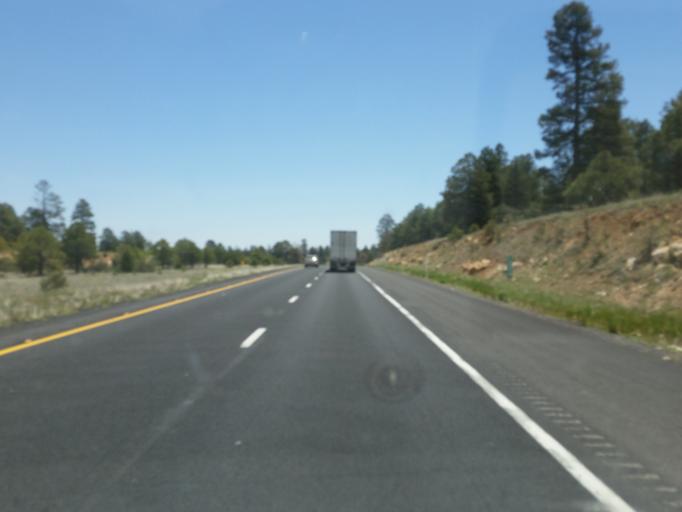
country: US
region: Arizona
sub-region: Coconino County
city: Flagstaff
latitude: 35.2119
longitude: -111.5323
